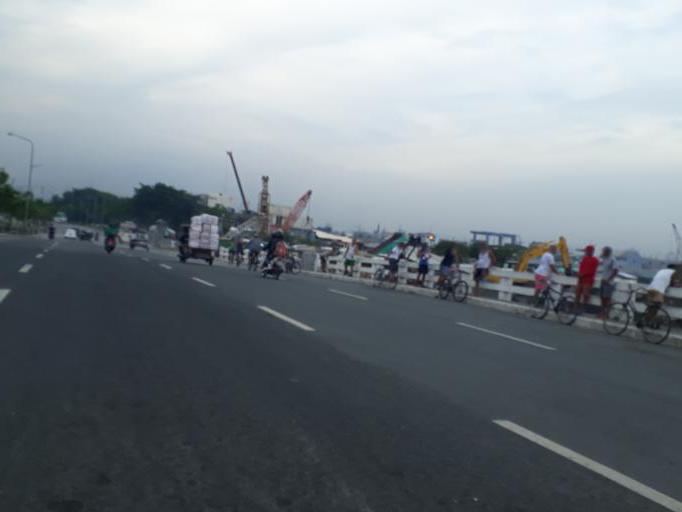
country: PH
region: Metro Manila
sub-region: Caloocan City
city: Niugan
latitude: 14.6501
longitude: 120.9483
